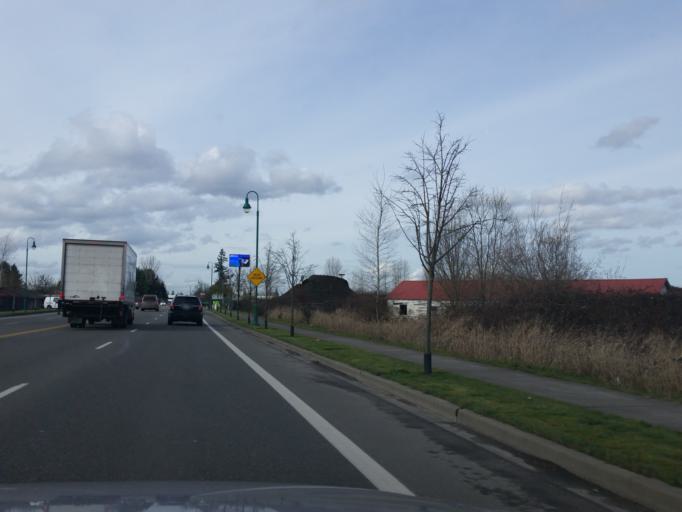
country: US
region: Washington
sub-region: Pierce County
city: Milton
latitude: 47.2239
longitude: -122.3268
